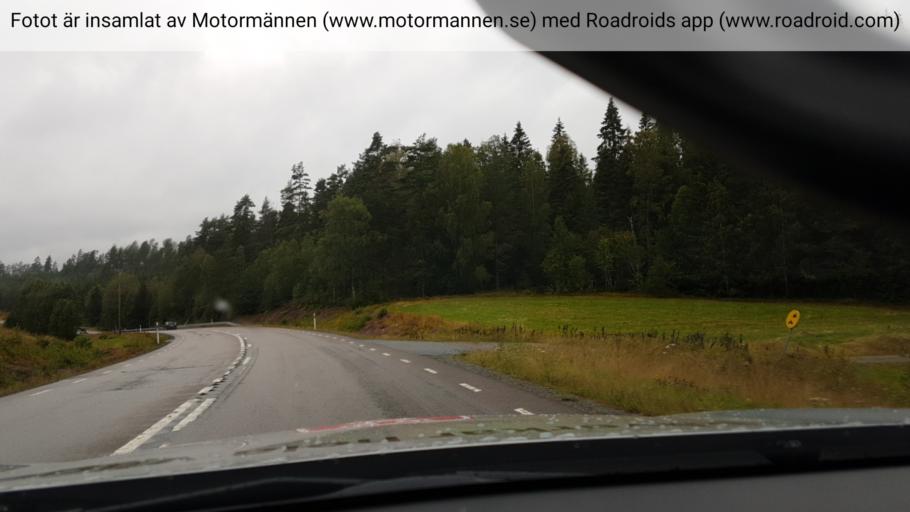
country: SE
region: Vaestra Goetaland
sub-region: Dals-Ed Kommun
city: Ed
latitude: 58.9362
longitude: 12.0714
